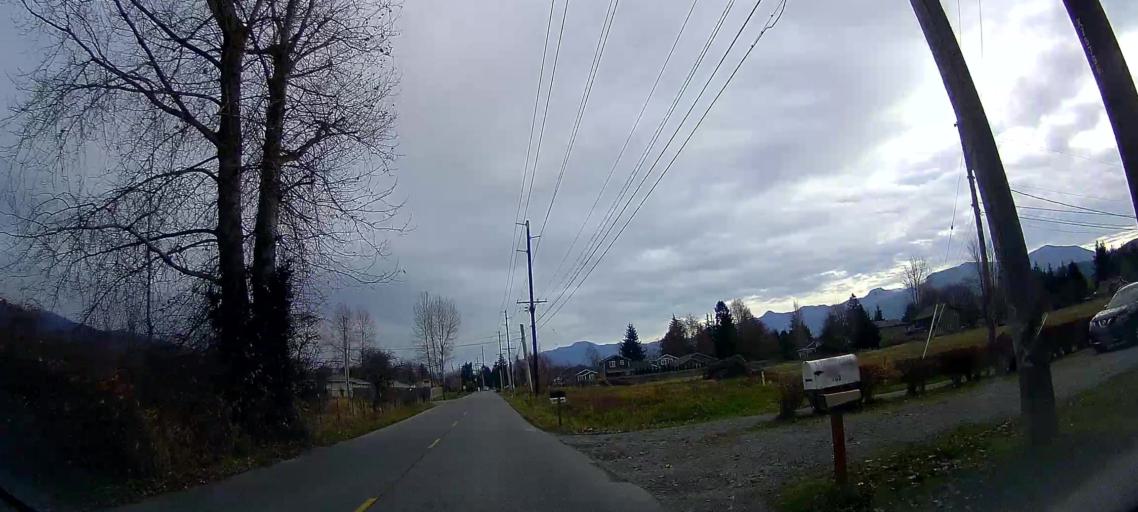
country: US
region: Washington
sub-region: Skagit County
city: Sedro-Woolley
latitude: 48.5146
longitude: -122.2518
